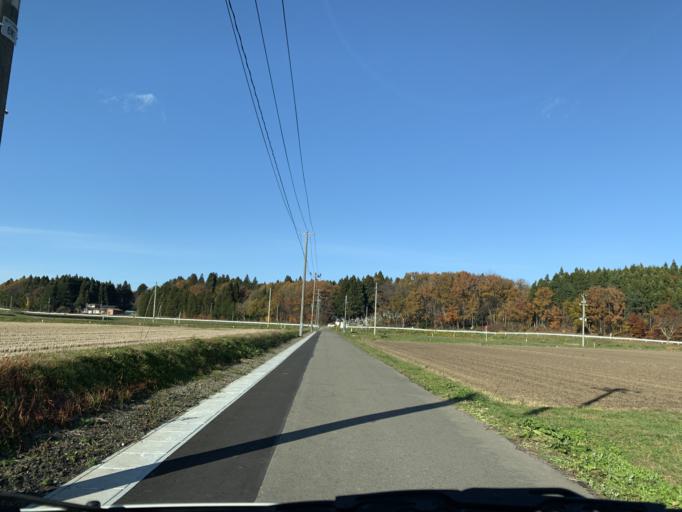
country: JP
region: Iwate
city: Kitakami
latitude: 39.2364
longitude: 141.0742
